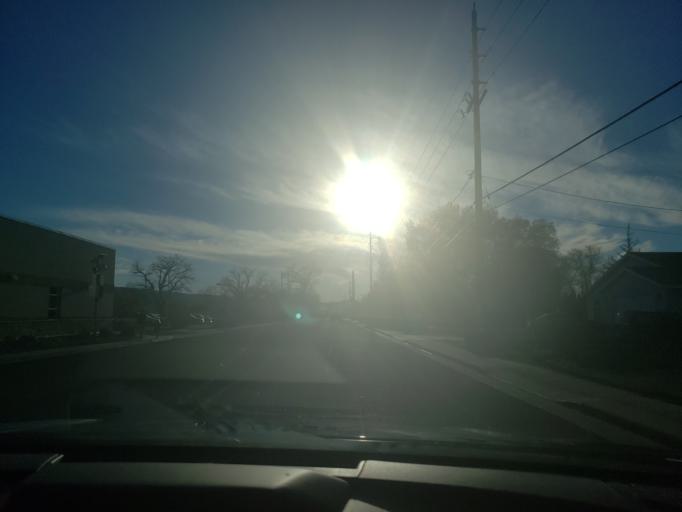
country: US
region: Colorado
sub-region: Mesa County
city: Fruita
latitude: 39.1644
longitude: -108.7366
